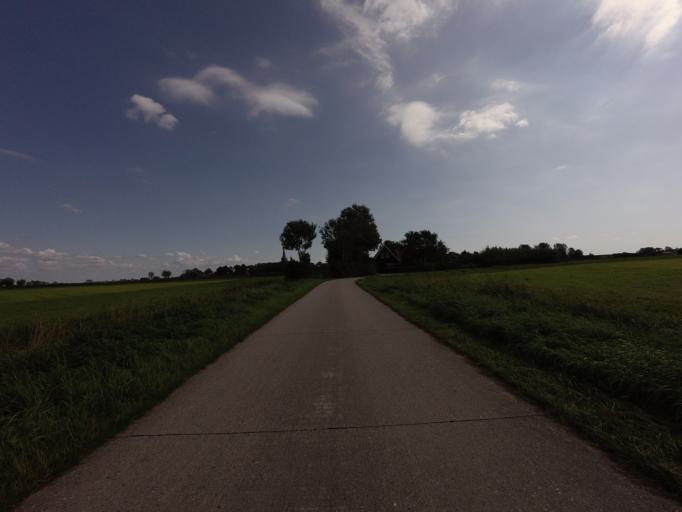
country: NL
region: Friesland
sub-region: Sudwest Fryslan
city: Scharnegoutum
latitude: 53.0790
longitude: 5.6319
